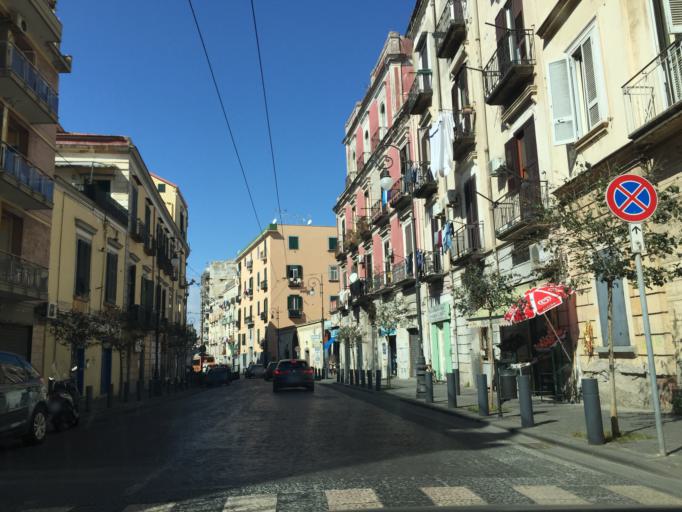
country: IT
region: Campania
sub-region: Provincia di Napoli
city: Portici
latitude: 40.8207
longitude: 14.3271
